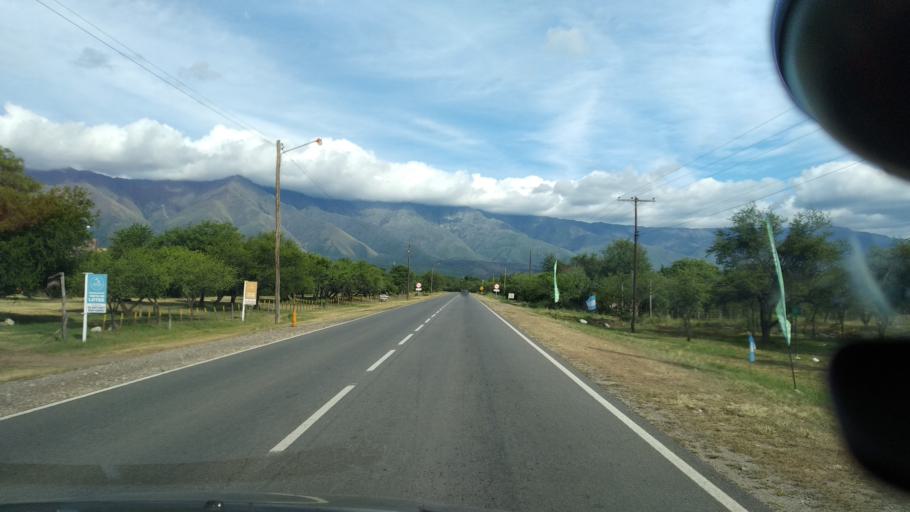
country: AR
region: Cordoba
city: Villa Las Rosas
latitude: -32.0084
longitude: -65.0555
